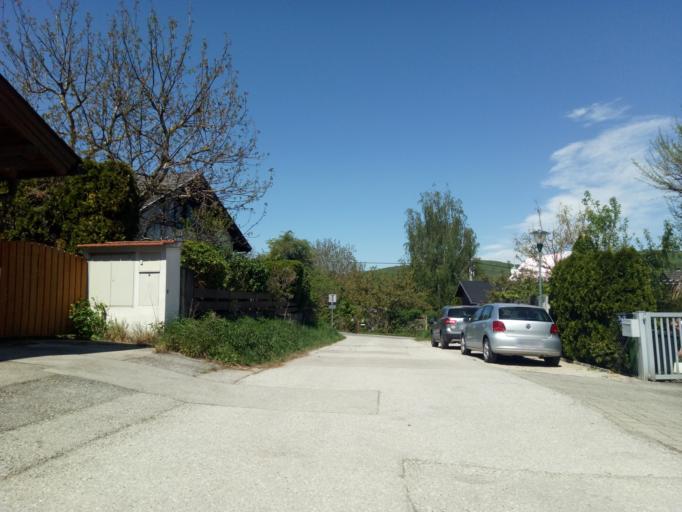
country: AT
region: Lower Austria
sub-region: Politischer Bezirk Modling
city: Kaltenleutgeben
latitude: 48.1275
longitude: 16.1869
